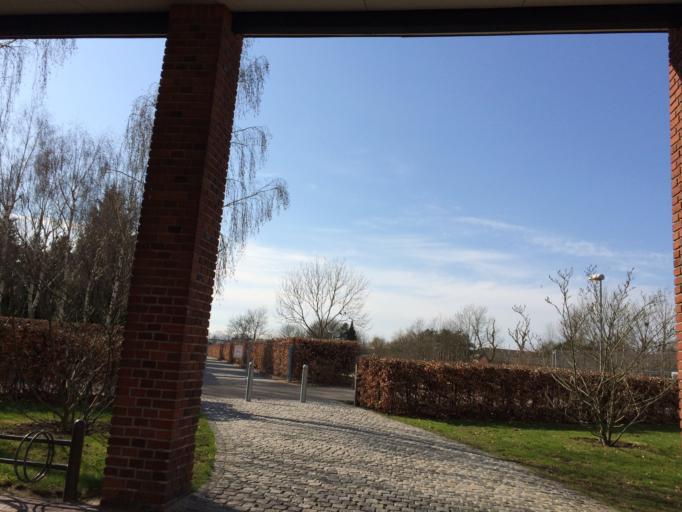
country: DK
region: Capital Region
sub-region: Hoje-Taastrup Kommune
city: Taastrup
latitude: 55.6418
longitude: 12.2931
